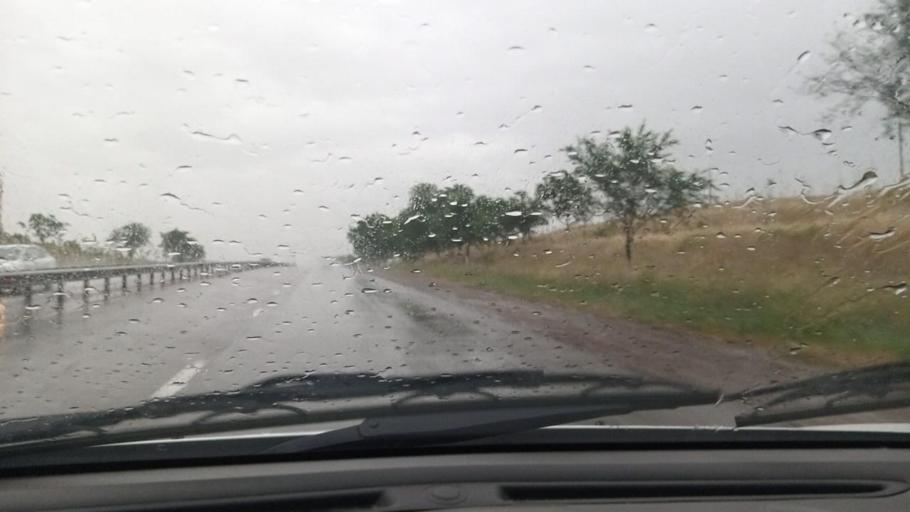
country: UZ
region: Toshkent
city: Ohangaron
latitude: 40.9647
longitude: 69.5535
